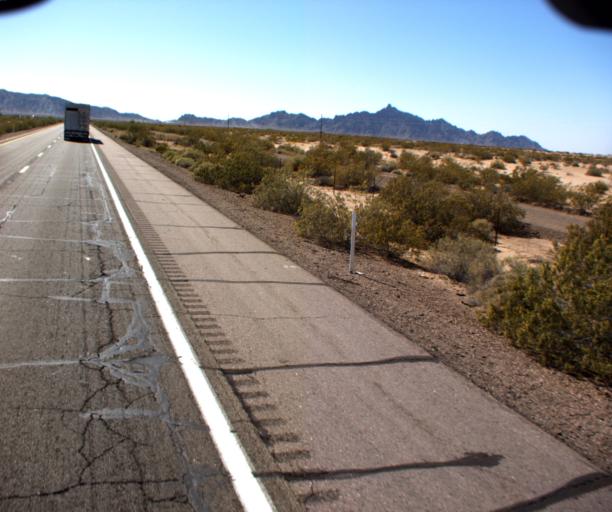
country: US
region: Arizona
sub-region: Yuma County
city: Wellton
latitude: 32.7468
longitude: -113.6728
